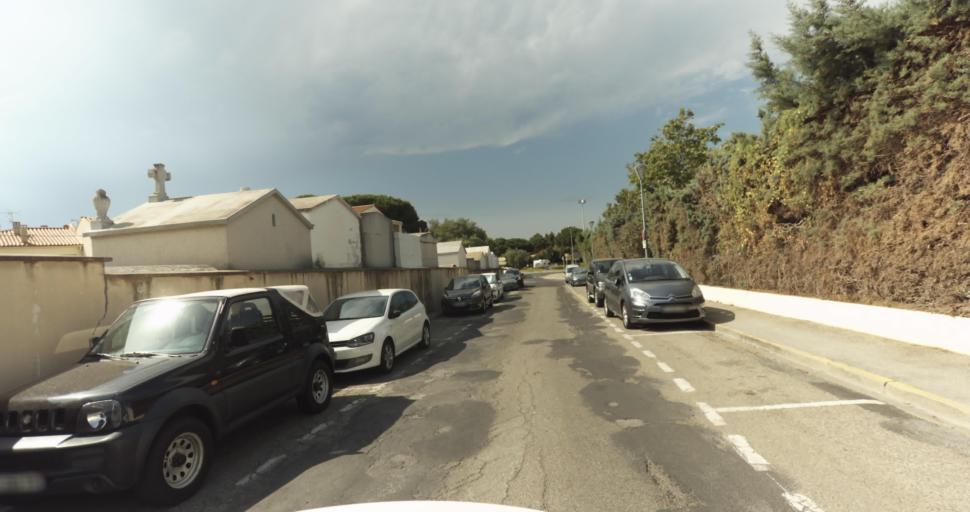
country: FR
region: Languedoc-Roussillon
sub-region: Departement des Pyrenees-Orientales
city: Elne
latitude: 42.6025
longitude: 2.9735
